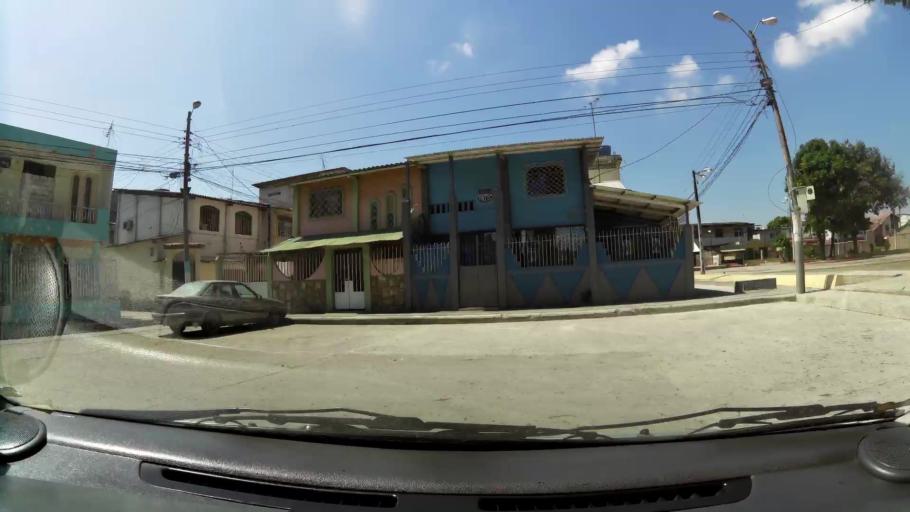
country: EC
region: Guayas
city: Guayaquil
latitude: -2.2346
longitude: -79.9005
